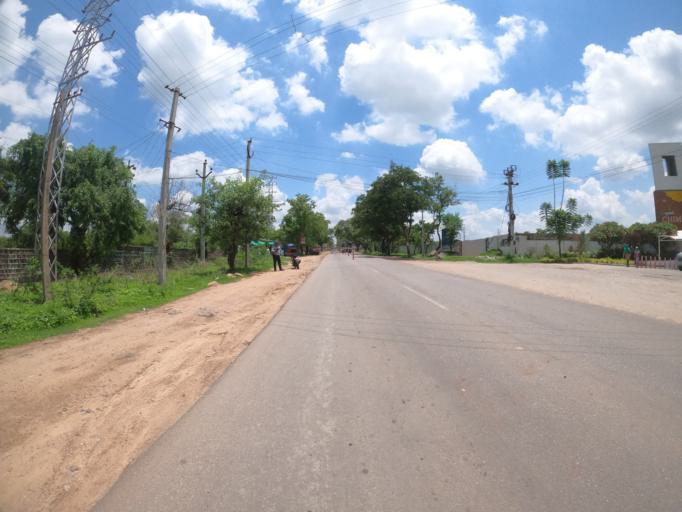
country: IN
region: Telangana
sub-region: Medak
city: Serilingampalle
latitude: 17.3855
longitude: 78.3324
